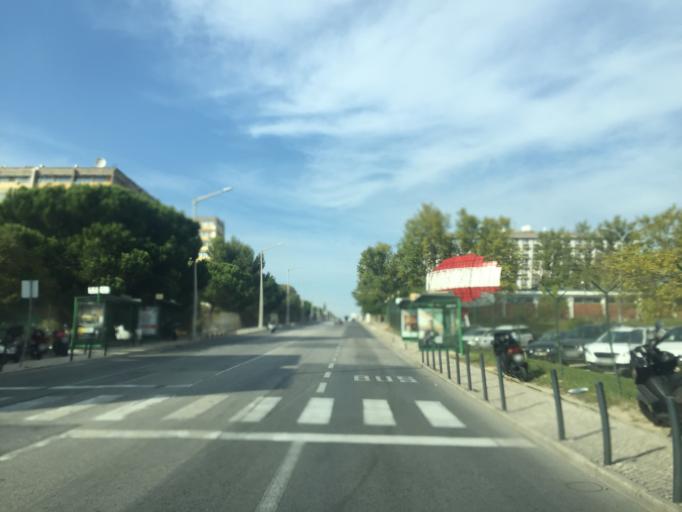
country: PT
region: Lisbon
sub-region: Loures
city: Moscavide
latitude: 38.7741
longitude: -9.1259
